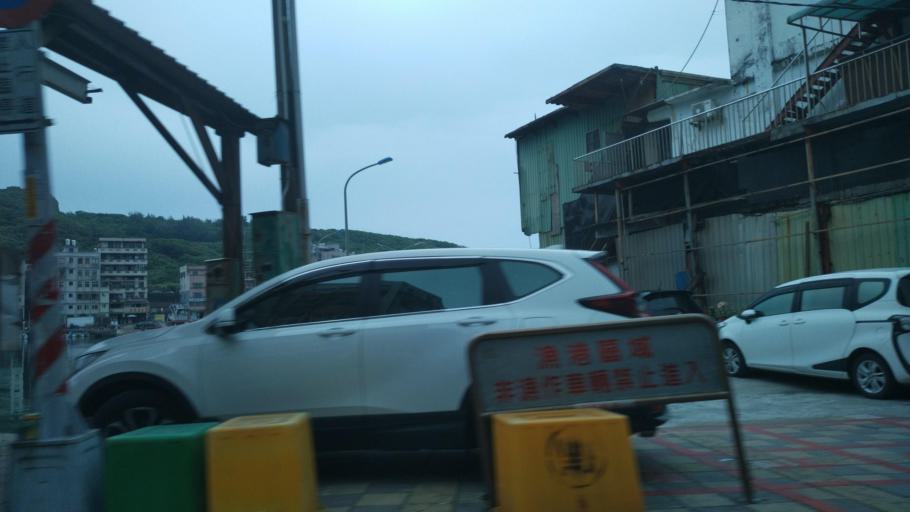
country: TW
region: Taiwan
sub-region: Keelung
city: Keelung
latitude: 25.2040
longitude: 121.6873
